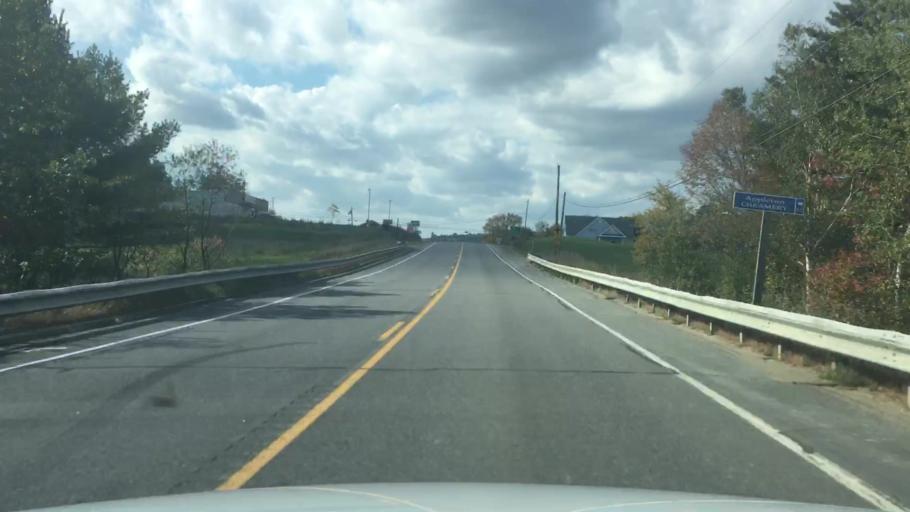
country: US
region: Maine
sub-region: Knox County
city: Union
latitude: 44.2163
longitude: -69.2724
